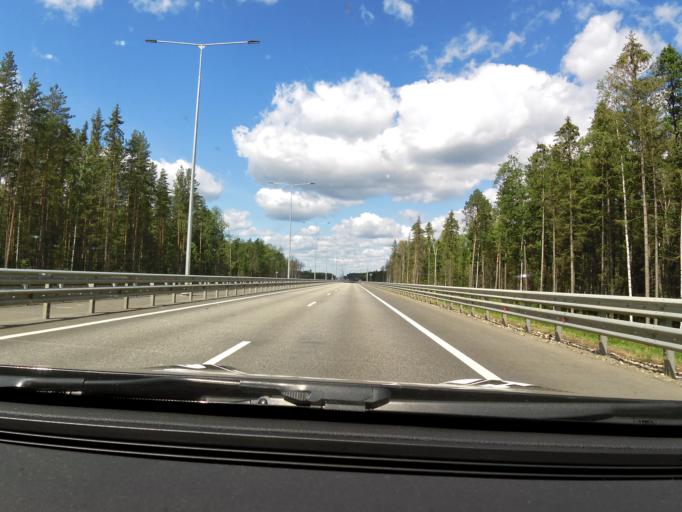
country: RU
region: Tverskaya
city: Krasnomayskiy
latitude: 57.4431
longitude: 34.4368
